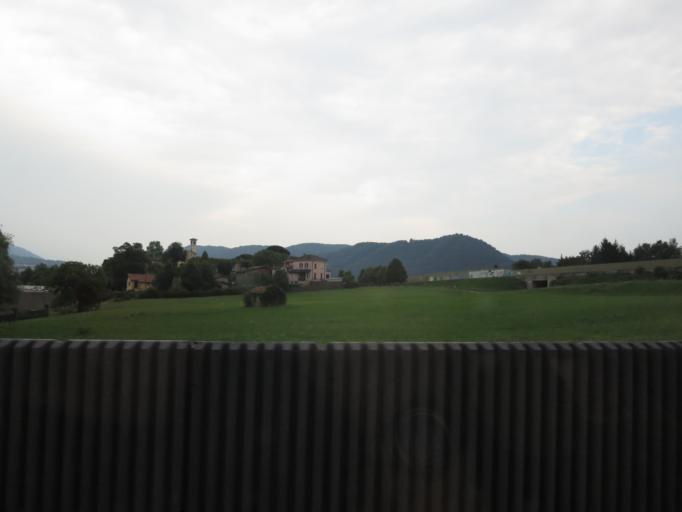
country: CH
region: Ticino
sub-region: Mendrisio District
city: Balerna
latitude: 45.8472
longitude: 8.9951
